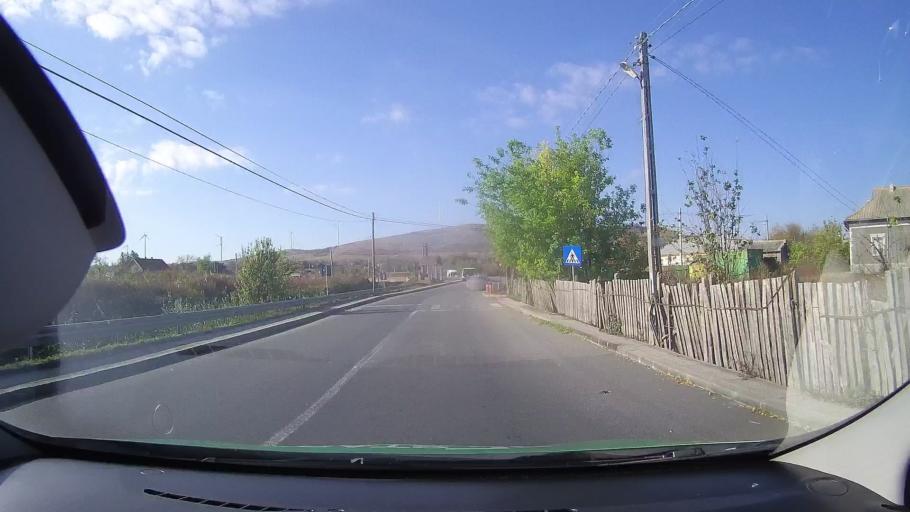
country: RO
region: Tulcea
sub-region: Comuna Valea Nucarilor
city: Agighiol
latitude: 45.0332
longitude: 28.8809
